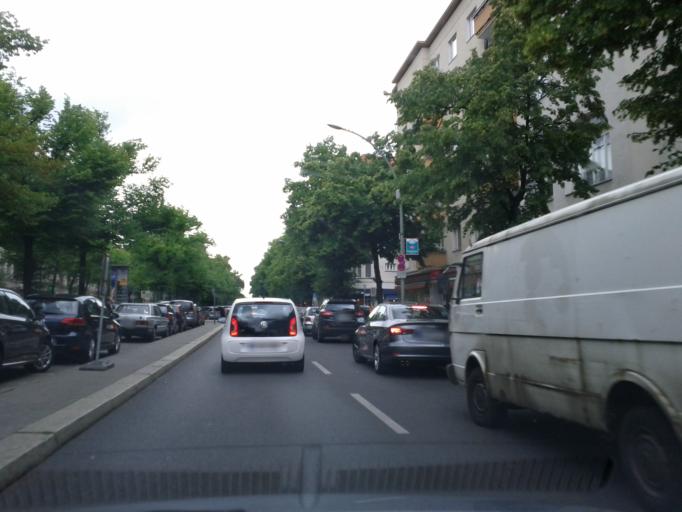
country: DE
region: Berlin
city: Westend
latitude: 52.5104
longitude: 13.2708
